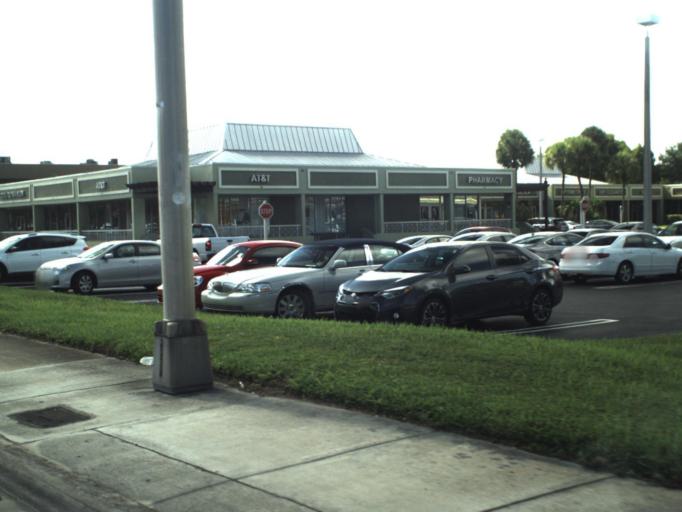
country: US
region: Florida
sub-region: Broward County
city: Hollywood
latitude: 26.0331
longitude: -80.1759
